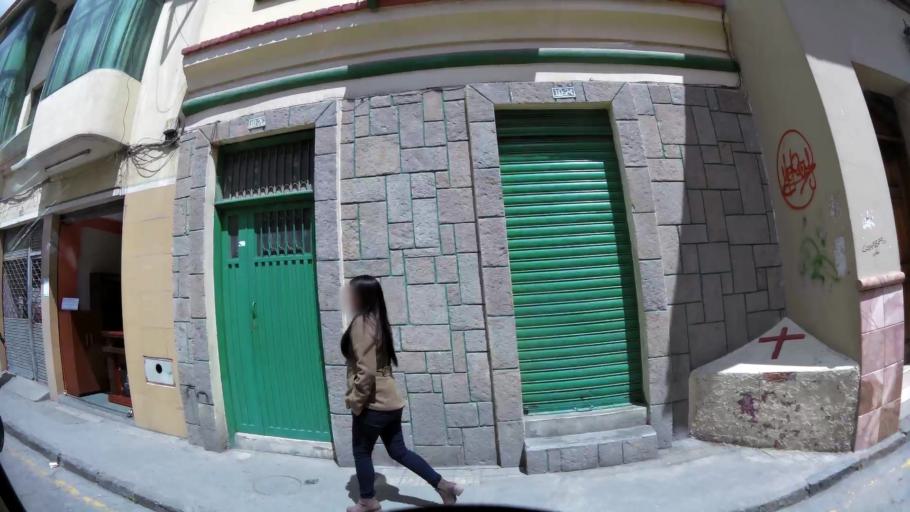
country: EC
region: Azuay
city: Cuenca
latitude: -2.8968
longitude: -78.9998
